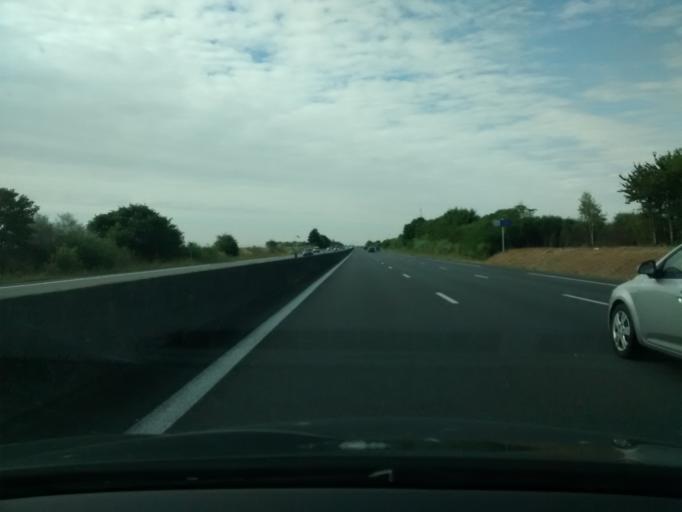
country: FR
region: Ile-de-France
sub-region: Departement de l'Essonne
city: Corbreuse
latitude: 48.4387
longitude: 1.9067
